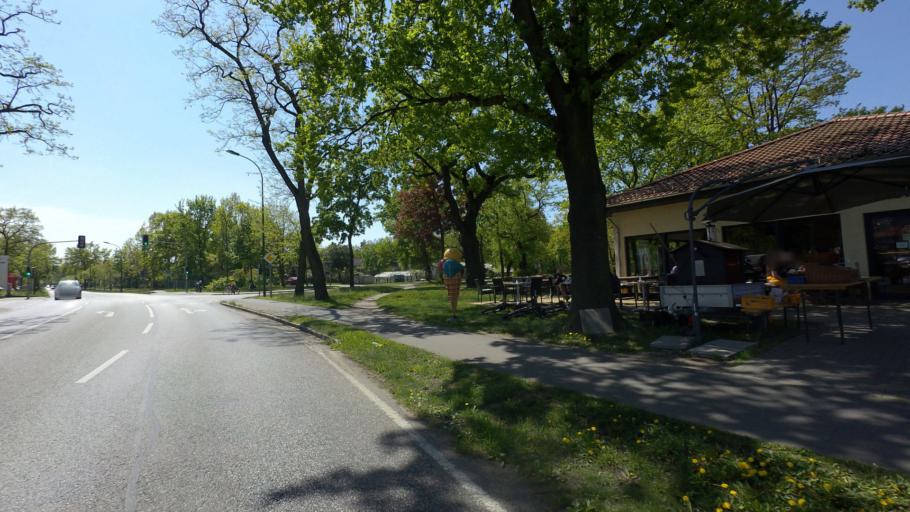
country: DE
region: Brandenburg
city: Konigs Wusterhausen
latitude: 52.2728
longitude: 13.6324
